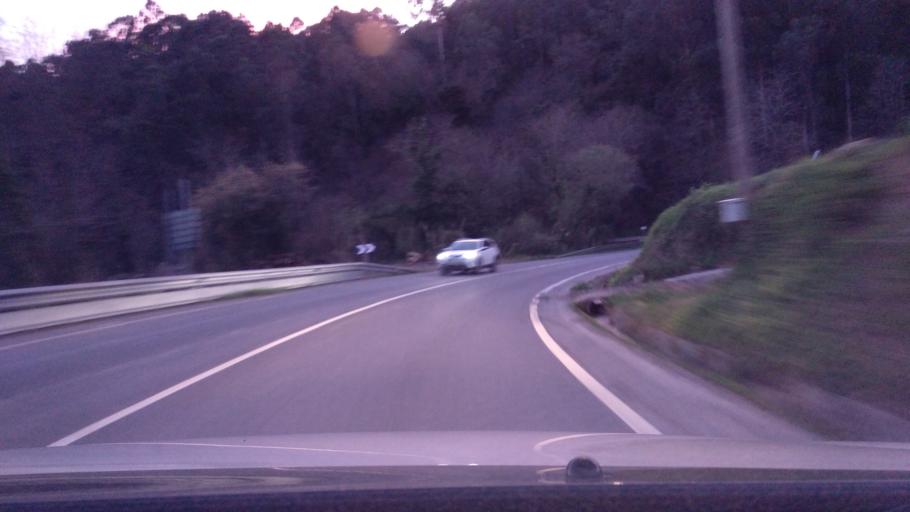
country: ES
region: Galicia
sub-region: Provincia de Pontevedra
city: Moana
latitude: 42.3060
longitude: -8.7429
